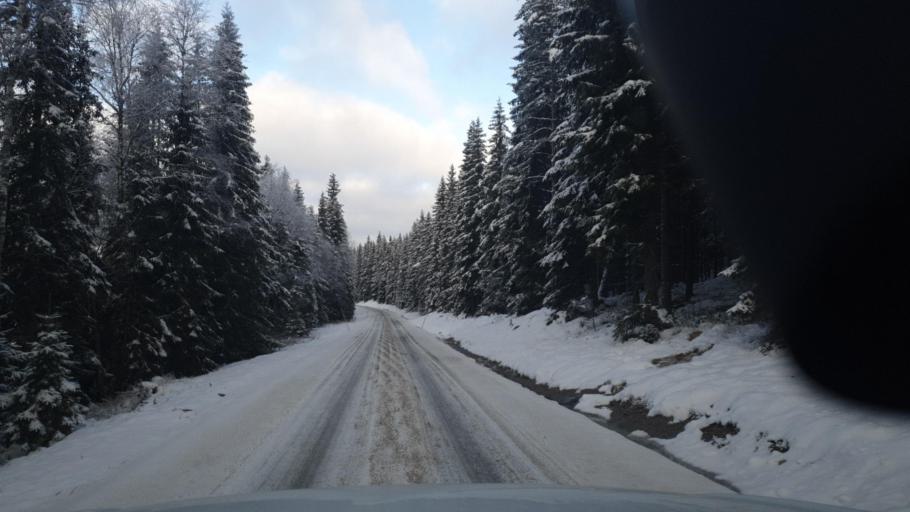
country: SE
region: Vaermland
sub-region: Eda Kommun
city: Charlottenberg
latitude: 60.0795
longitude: 12.6197
